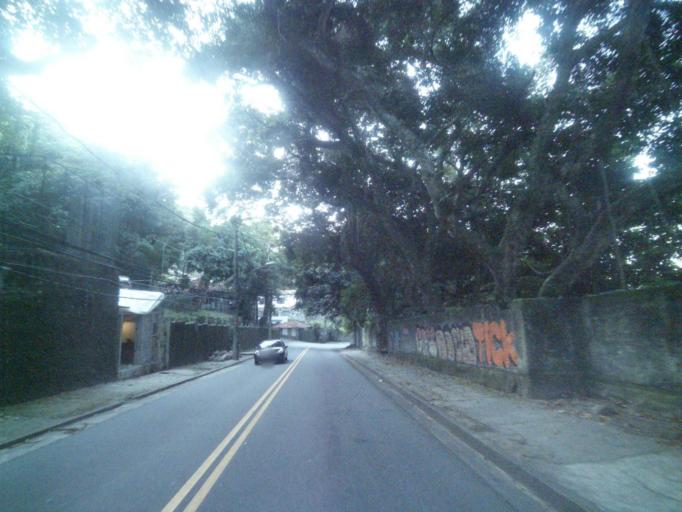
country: BR
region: Rio de Janeiro
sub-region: Rio De Janeiro
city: Rio de Janeiro
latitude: -23.0022
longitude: -43.2768
